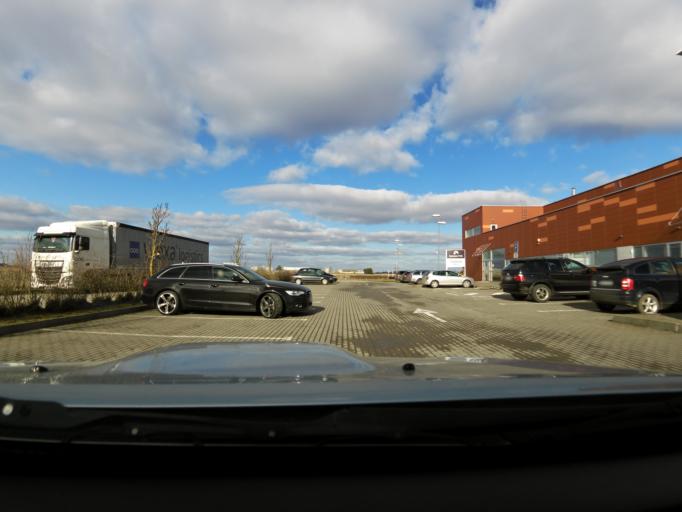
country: LT
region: Panevezys
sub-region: Panevezys City
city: Panevezys
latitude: 55.6706
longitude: 24.3496
